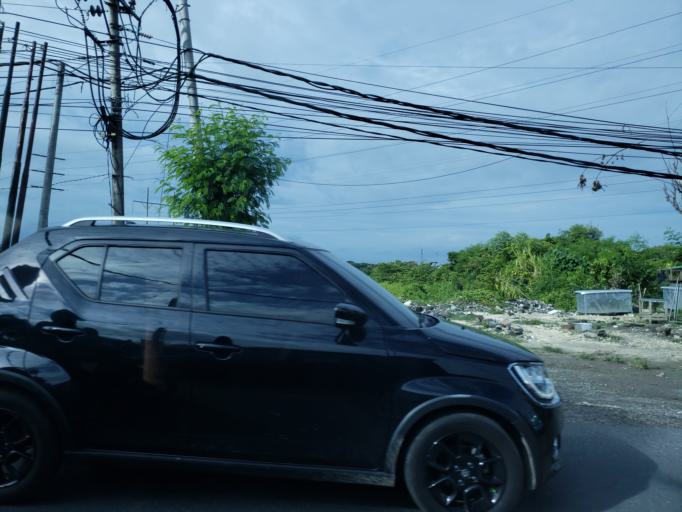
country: ID
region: Bali
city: Karyadharma
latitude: -8.6801
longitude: 115.1880
